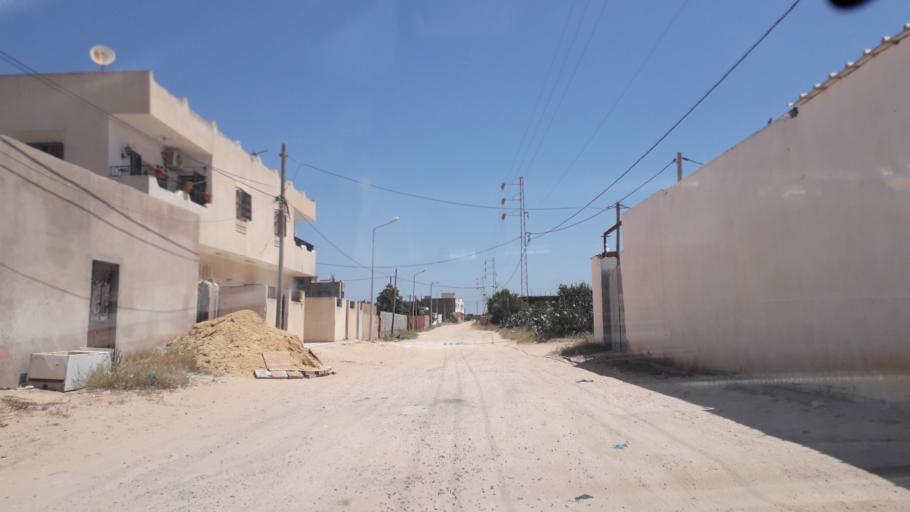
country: TN
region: Safaqis
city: Al Qarmadah
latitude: 34.8281
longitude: 10.7736
